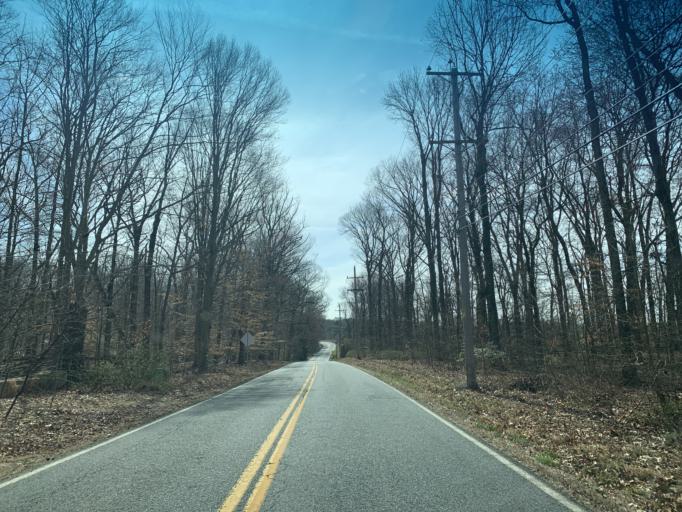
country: US
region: Maryland
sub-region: Cecil County
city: Charlestown
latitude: 39.5634
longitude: -76.0208
